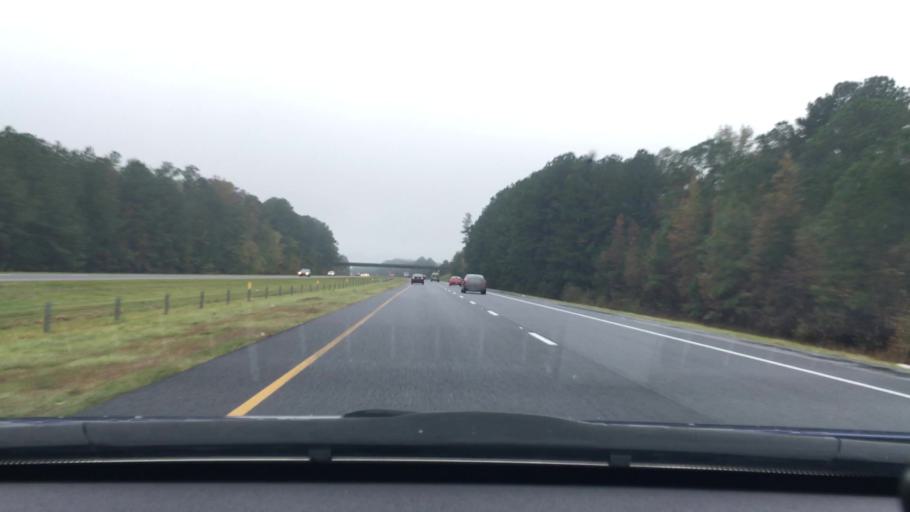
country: US
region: South Carolina
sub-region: Lee County
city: Bishopville
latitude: 34.1947
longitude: -80.1346
